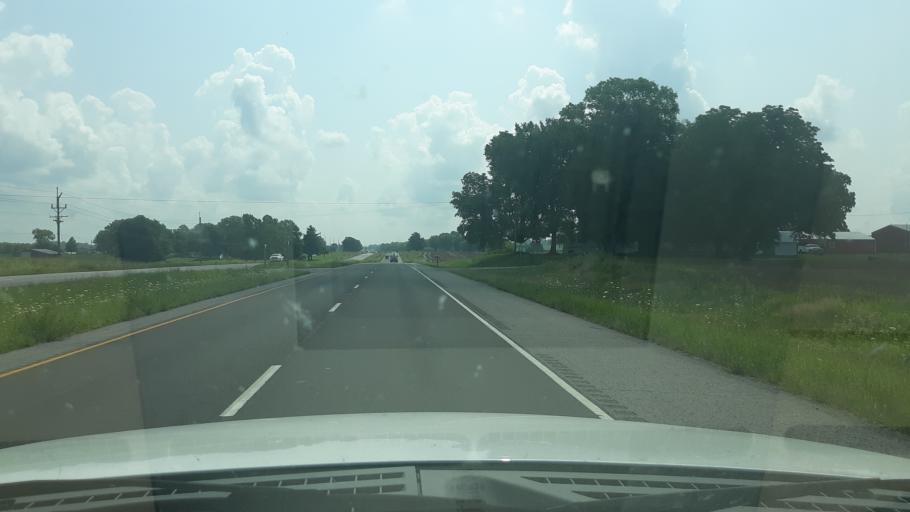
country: US
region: Illinois
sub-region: Williamson County
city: Marion
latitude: 37.7292
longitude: -88.8651
